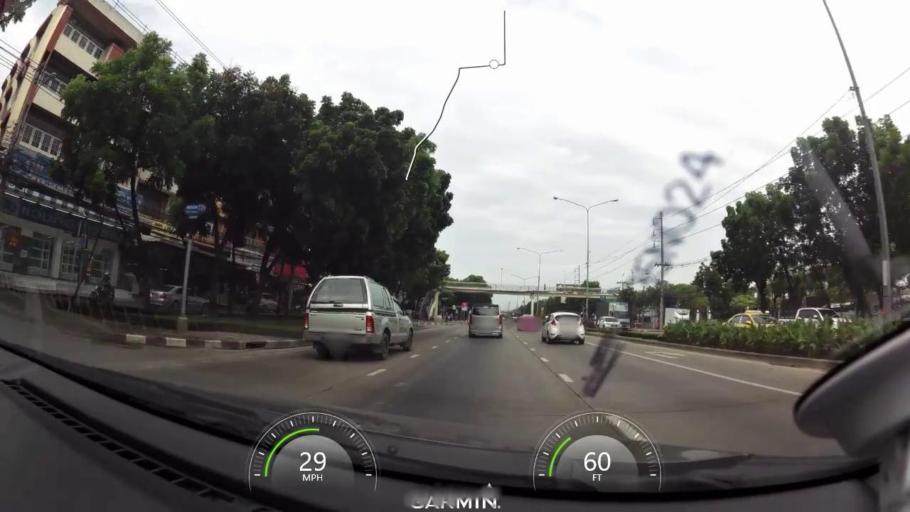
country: TH
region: Bangkok
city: Nong Khaem
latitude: 13.7065
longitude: 100.3570
